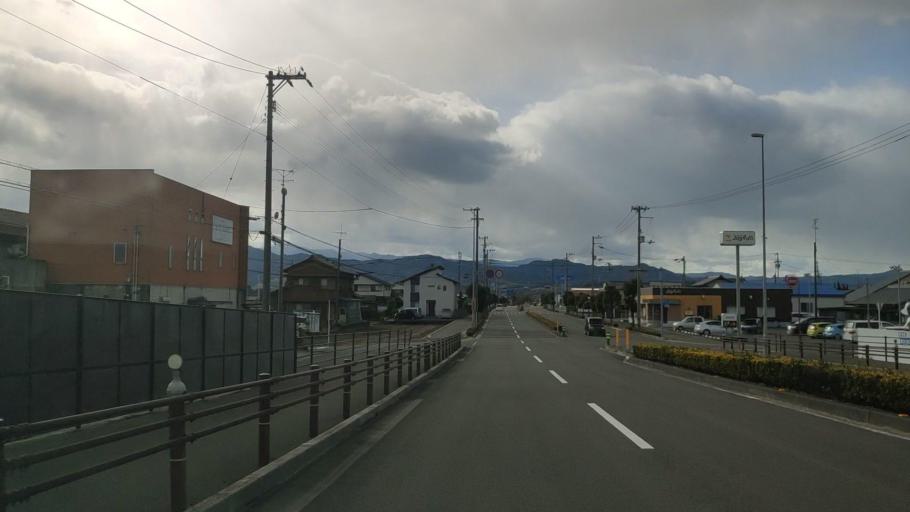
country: JP
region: Ehime
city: Saijo
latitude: 34.0436
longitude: 133.0039
